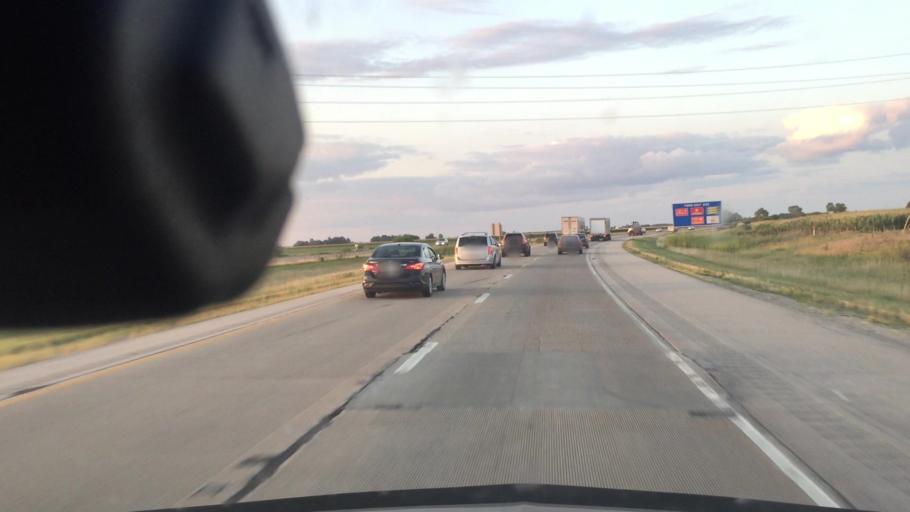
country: US
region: Illinois
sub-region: Livingston County
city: Dwight
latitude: 41.1092
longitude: -88.4457
